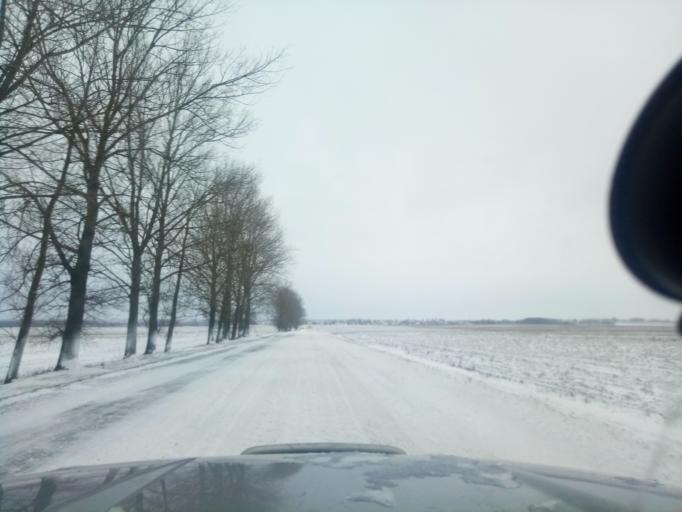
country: BY
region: Minsk
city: Tsimkavichy
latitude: 53.0558
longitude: 26.9528
